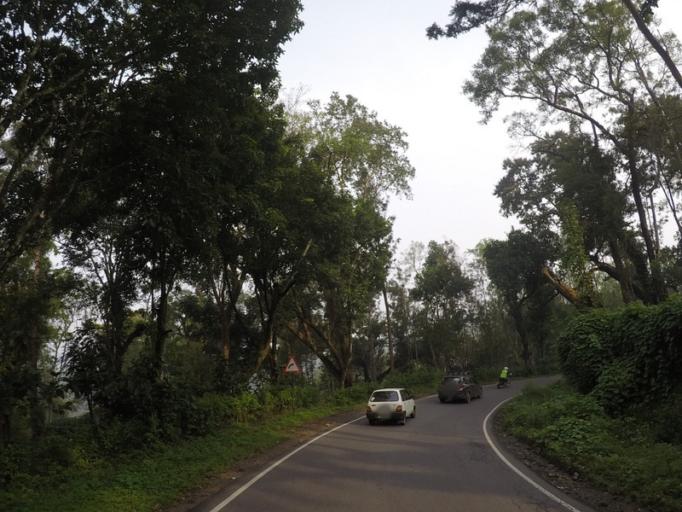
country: IN
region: Karnataka
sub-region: Chikmagalur
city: Mudigere
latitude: 13.2668
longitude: 75.6239
